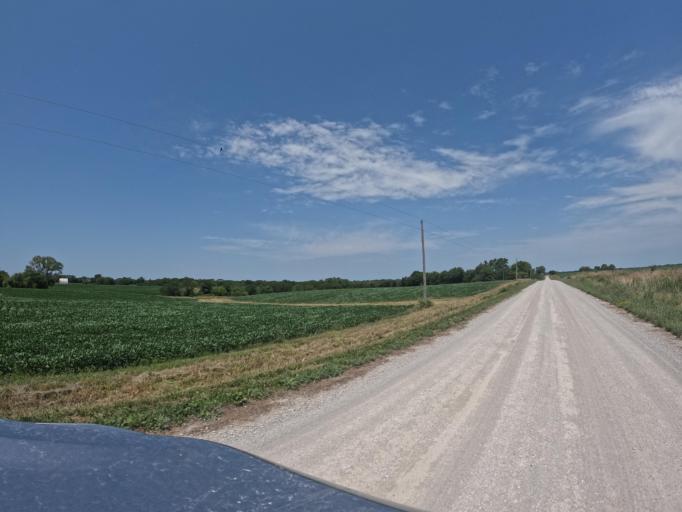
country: US
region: Iowa
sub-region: Appanoose County
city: Centerville
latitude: 40.7876
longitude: -92.9160
